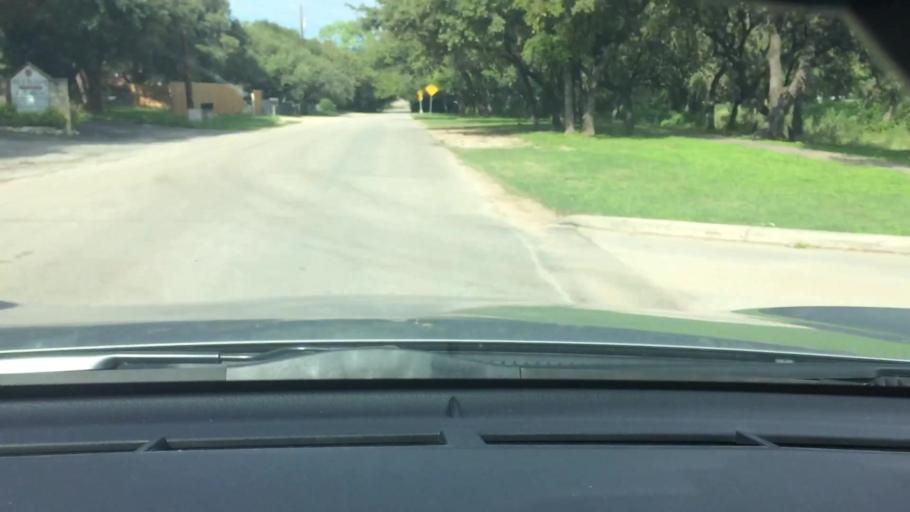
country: US
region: Texas
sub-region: Bexar County
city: Shavano Park
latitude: 29.5512
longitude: -98.5651
